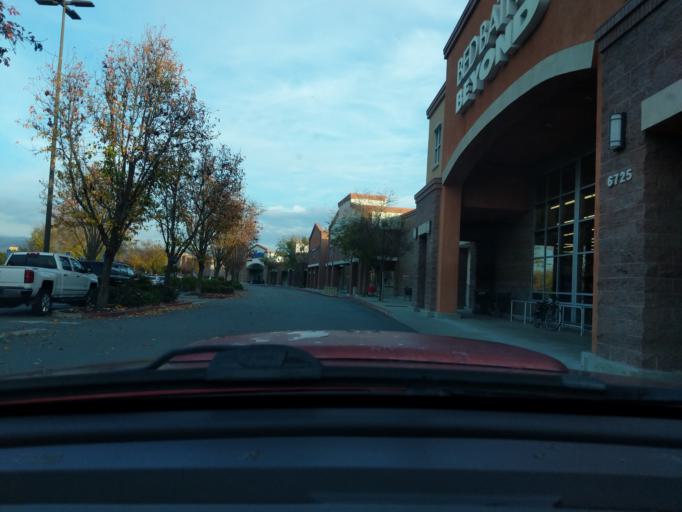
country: US
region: California
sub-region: Santa Clara County
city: Gilroy
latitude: 37.0003
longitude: -121.5534
